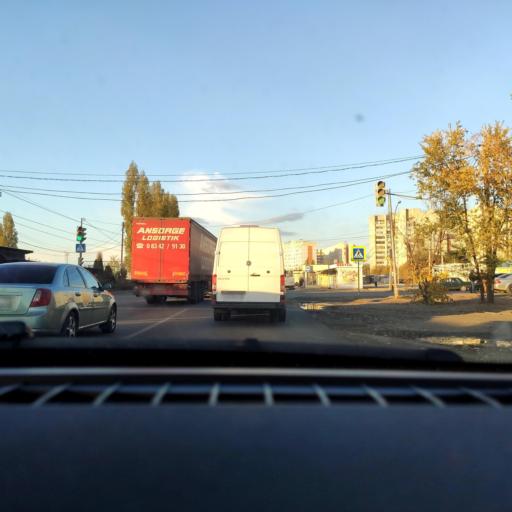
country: RU
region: Voronezj
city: Voronezh
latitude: 51.6410
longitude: 39.2658
